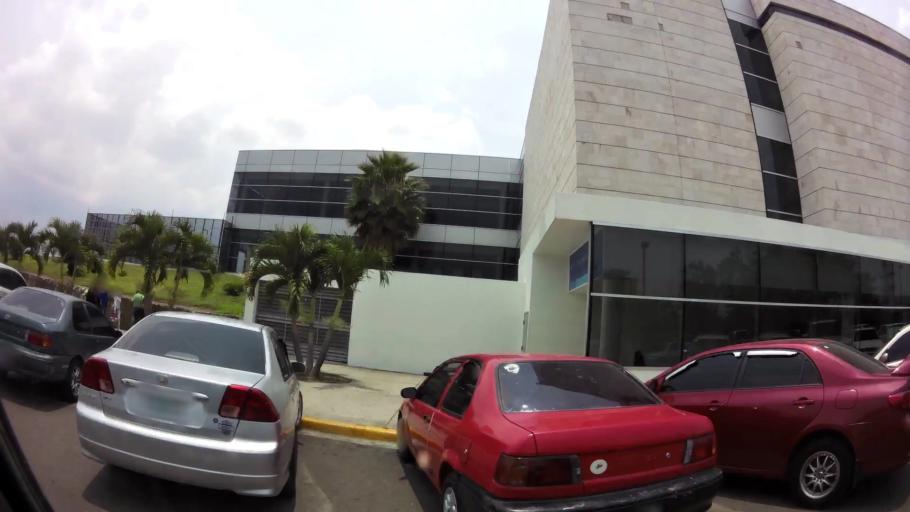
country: HN
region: Francisco Morazan
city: Tegucigalpa
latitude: 14.0613
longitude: -87.2194
